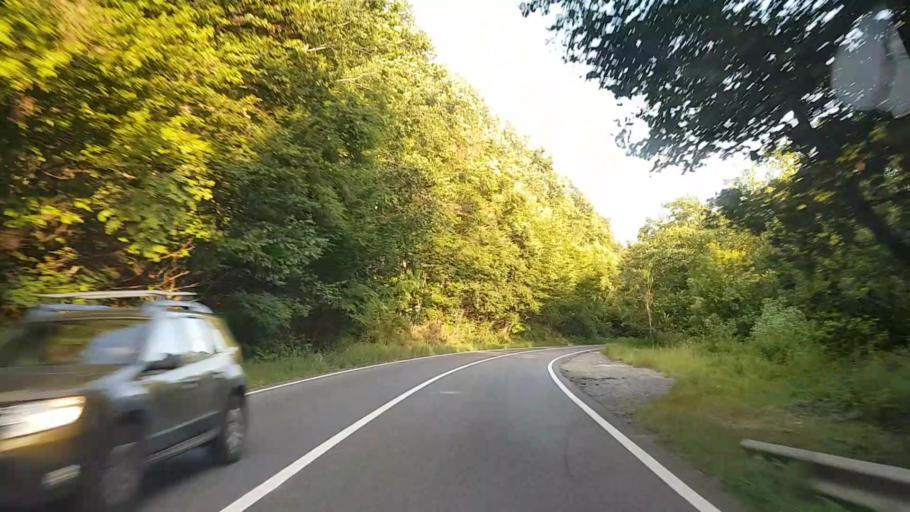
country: RO
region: Harghita
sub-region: Comuna Corund
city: Corund
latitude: 46.4373
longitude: 25.2305
